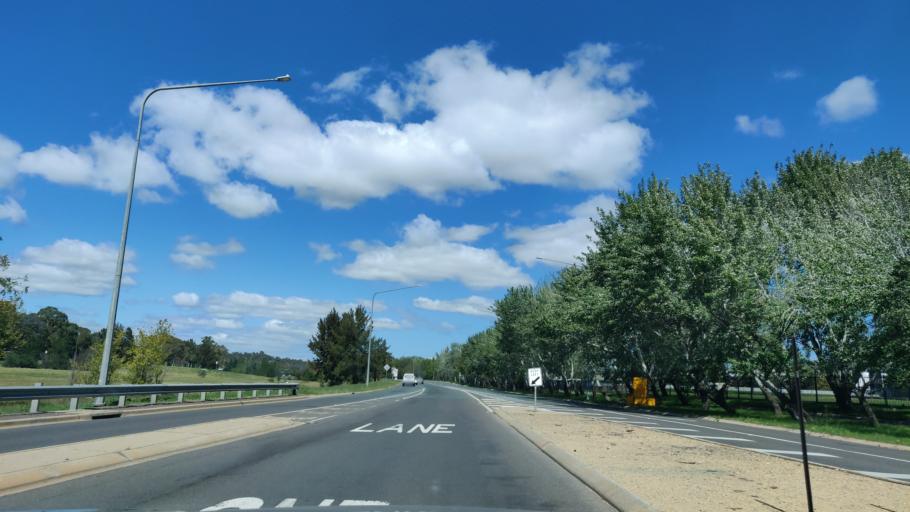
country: AU
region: Australian Capital Territory
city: Forrest
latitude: -35.3577
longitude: 149.0917
